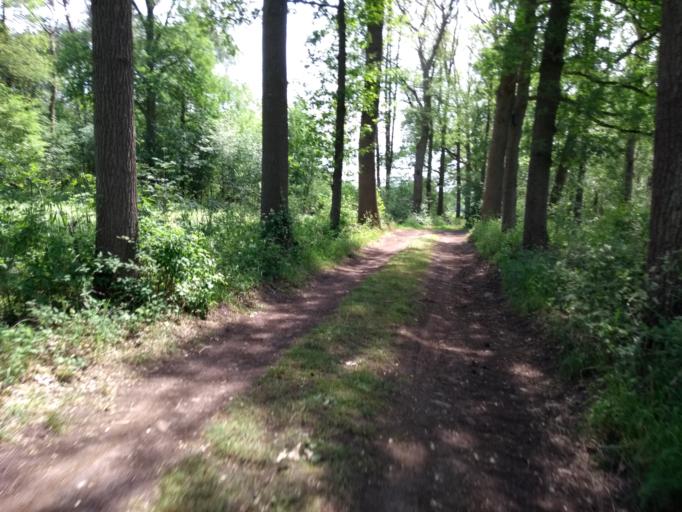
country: NL
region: Overijssel
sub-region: Gemeente Almelo
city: Almelo
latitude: 52.3638
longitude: 6.7095
